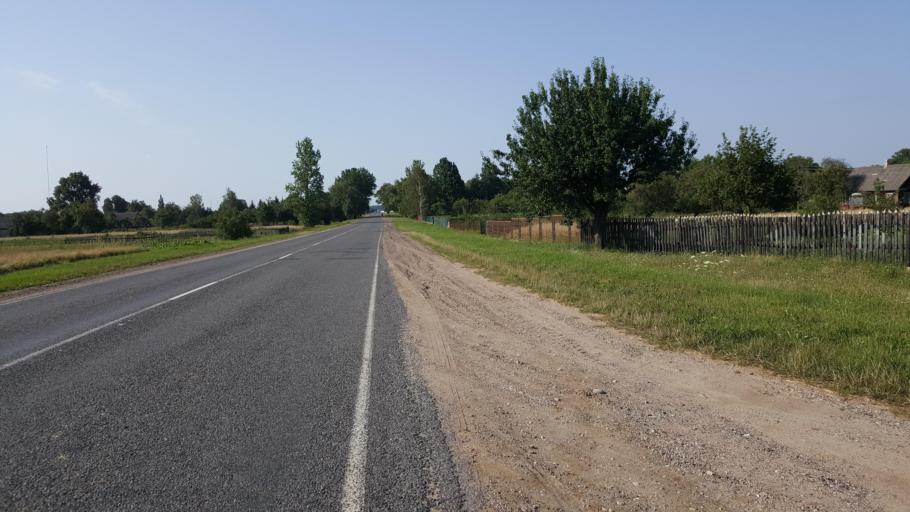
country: BY
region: Brest
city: Kamyanyets
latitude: 52.3112
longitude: 23.9217
